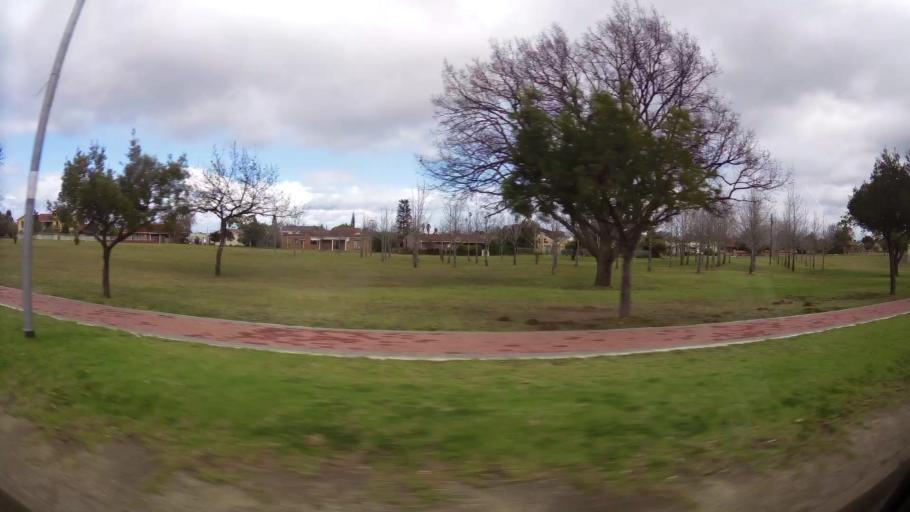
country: ZA
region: Western Cape
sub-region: Eden District Municipality
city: George
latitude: -33.9660
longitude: 22.4835
